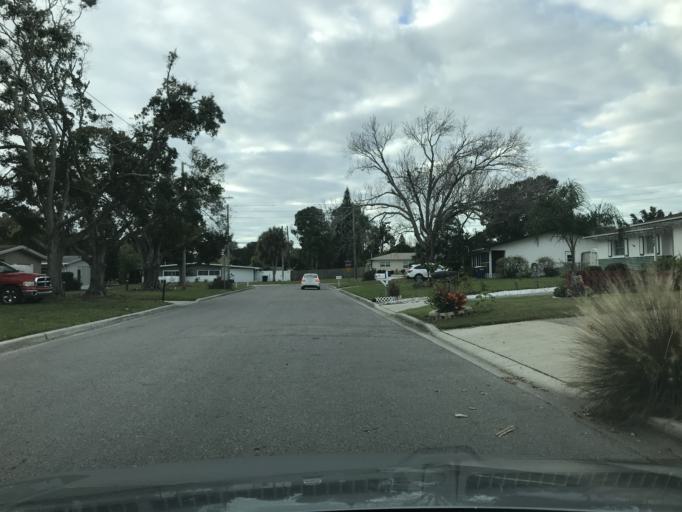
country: US
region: Florida
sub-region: Pinellas County
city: Belleair
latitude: 27.9451
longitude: -82.7840
